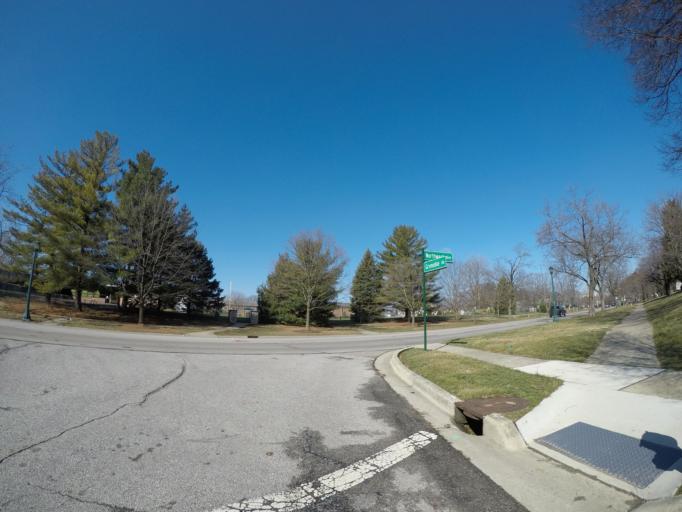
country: US
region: Ohio
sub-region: Franklin County
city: Upper Arlington
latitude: 40.0009
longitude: -83.0547
